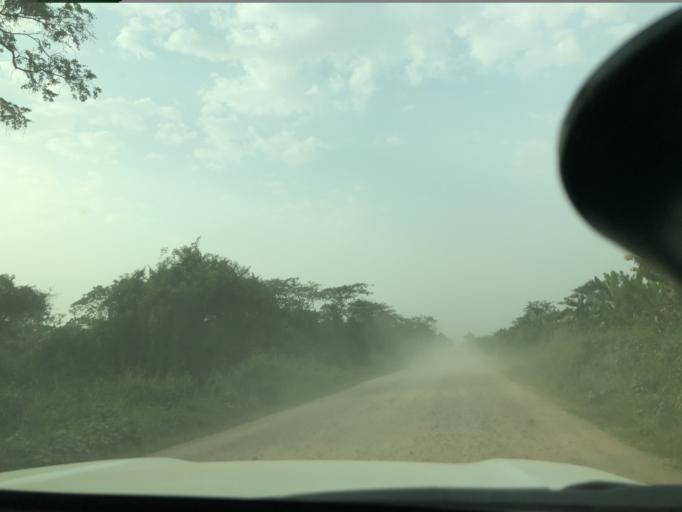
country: UG
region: Western Region
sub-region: Kasese District
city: Margherita
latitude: 0.2655
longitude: 29.6763
